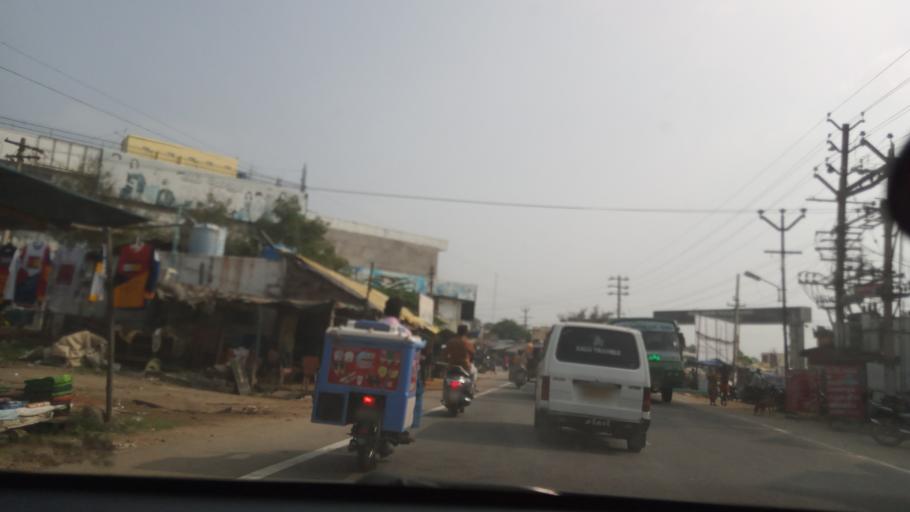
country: IN
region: Tamil Nadu
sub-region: Erode
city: Punjai Puliyampatti
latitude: 11.3489
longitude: 77.1657
